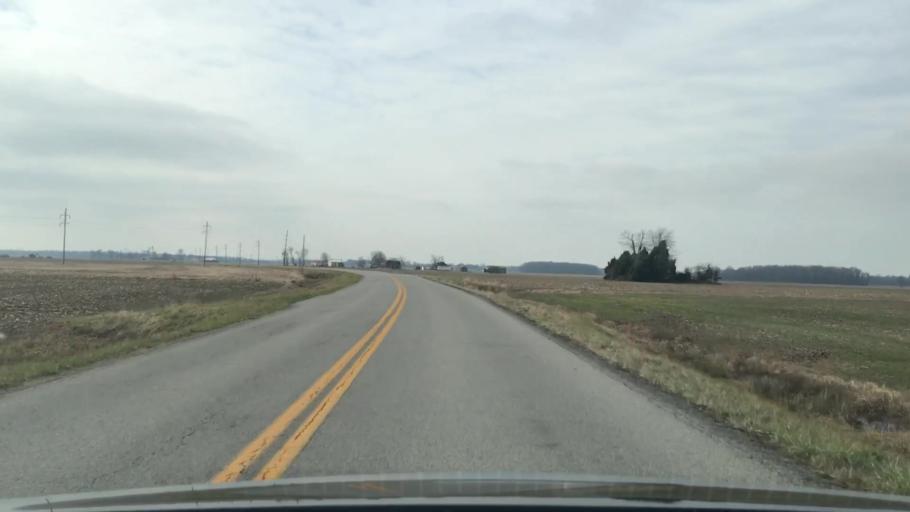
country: US
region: Kentucky
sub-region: McLean County
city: Calhoun
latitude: 37.5343
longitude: -87.3168
